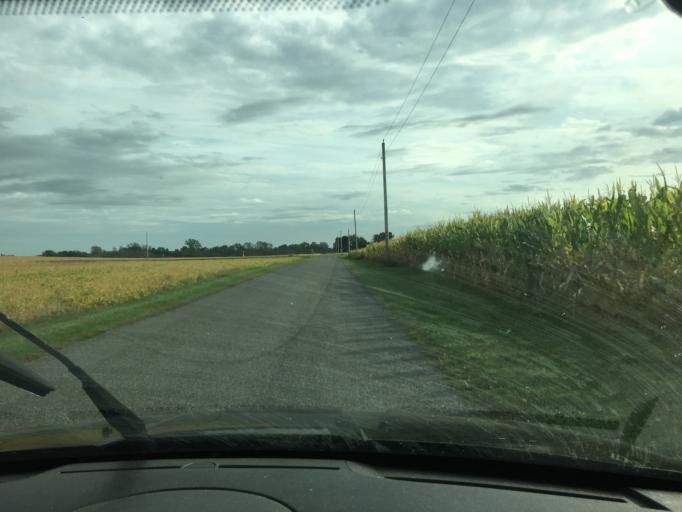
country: US
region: Ohio
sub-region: Logan County
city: Bellefontaine
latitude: 40.3220
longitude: -83.8061
